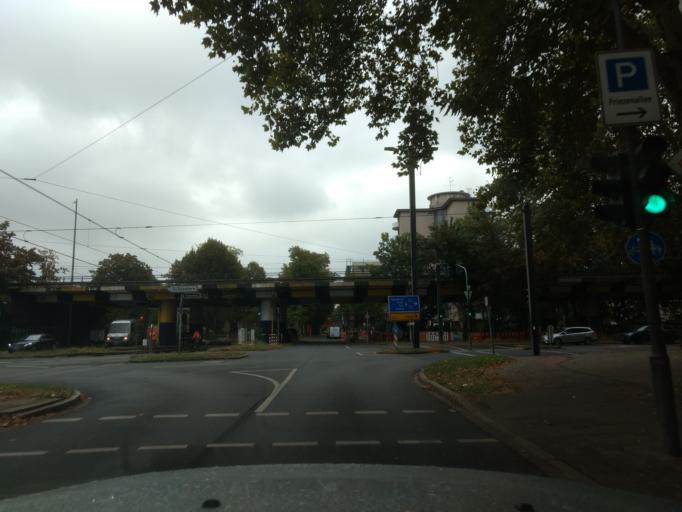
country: DE
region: North Rhine-Westphalia
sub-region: Regierungsbezirk Dusseldorf
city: Dusseldorf
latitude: 51.2379
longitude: 6.7347
